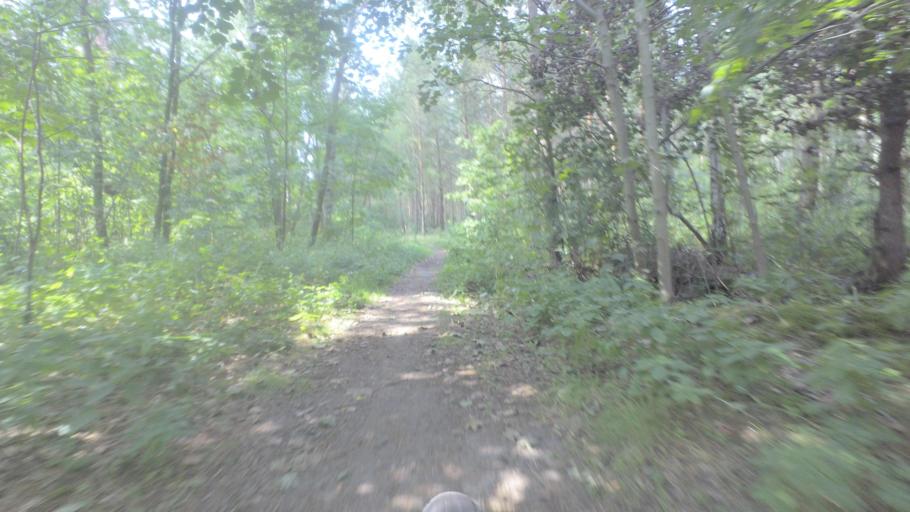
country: DE
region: Brandenburg
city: Ludwigsfelde
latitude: 52.3166
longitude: 13.2507
